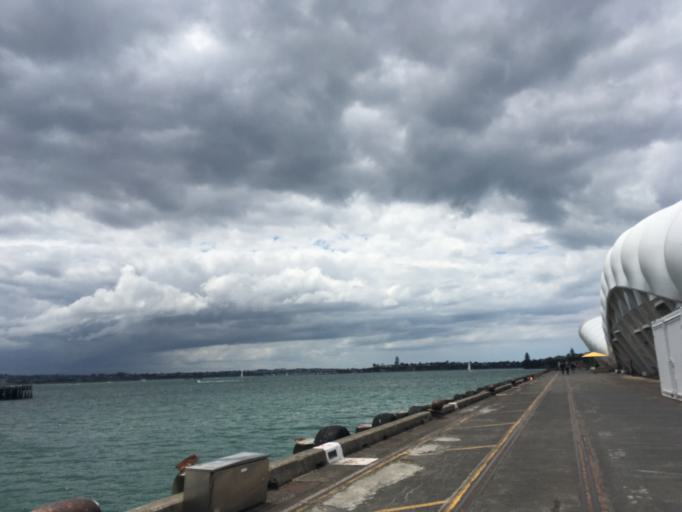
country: NZ
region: Auckland
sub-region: Auckland
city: Auckland
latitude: -36.8414
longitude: 174.7677
